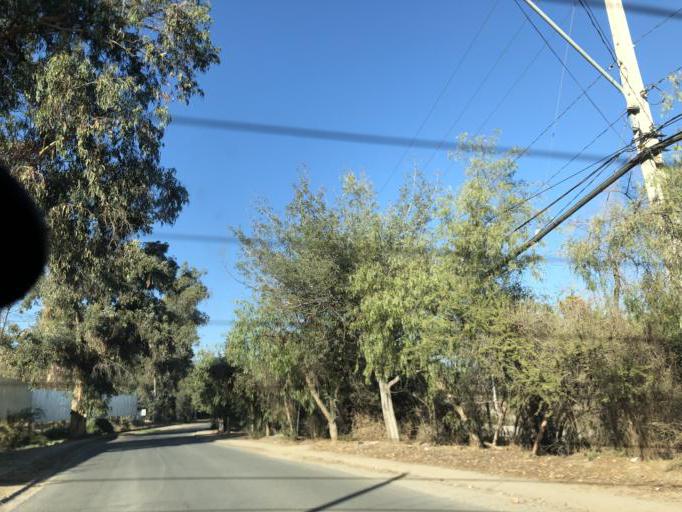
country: CL
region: Santiago Metropolitan
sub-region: Provincia de Cordillera
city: Puente Alto
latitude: -33.5583
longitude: -70.5349
